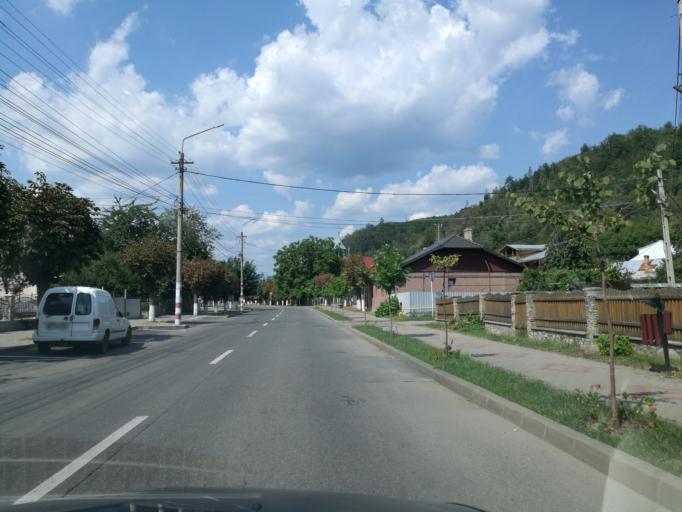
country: RO
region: Neamt
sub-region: Oras Targu Neamt
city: Humulesti
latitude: 47.2075
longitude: 26.3568
